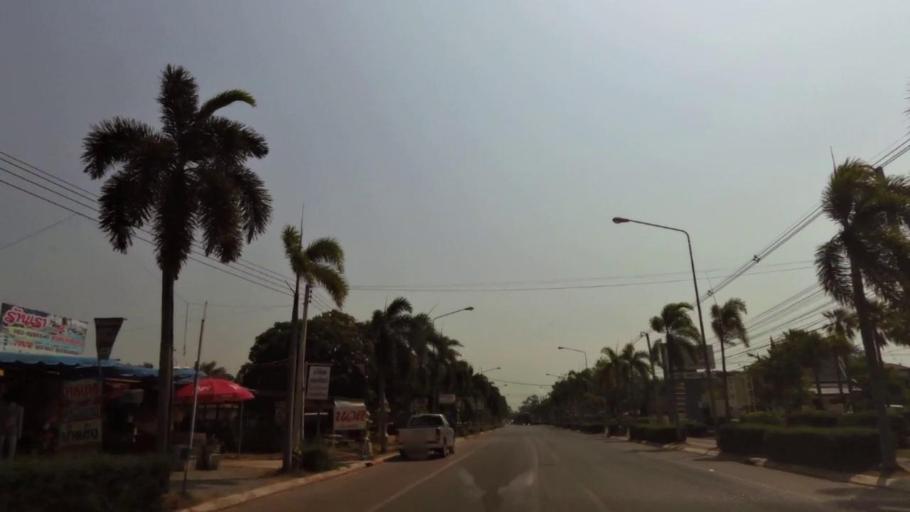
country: TH
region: Chanthaburi
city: Tha Mai
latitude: 12.5534
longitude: 101.9219
